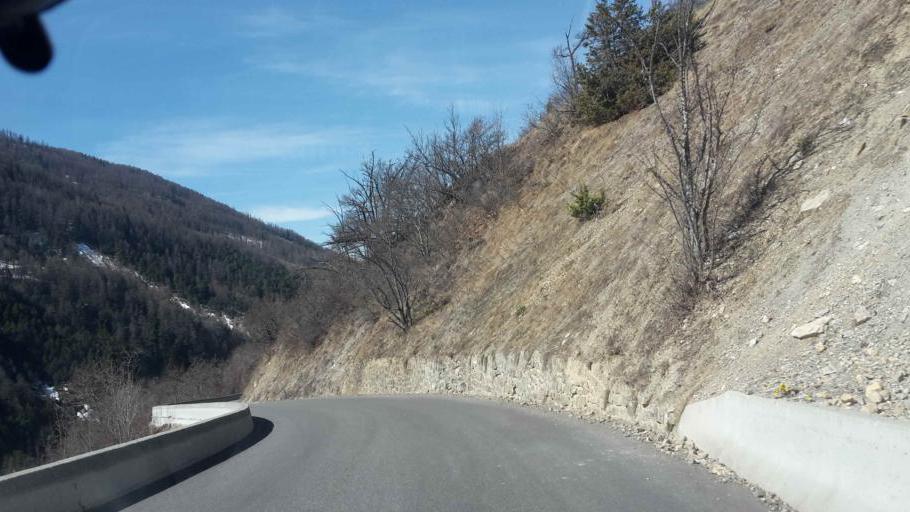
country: FR
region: Provence-Alpes-Cote d'Azur
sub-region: Departement des Hautes-Alpes
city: Embrun
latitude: 44.5503
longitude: 6.5890
